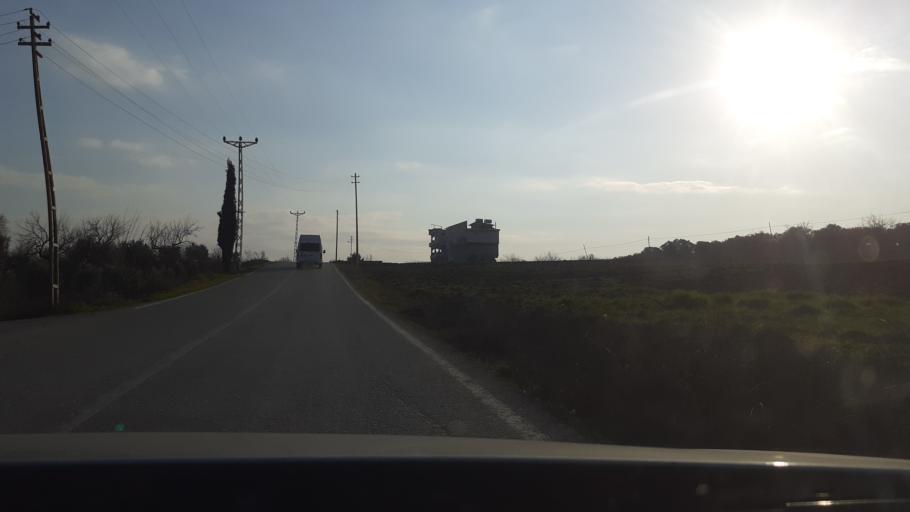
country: TR
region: Hatay
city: Boynuyogun
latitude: 36.1364
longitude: 36.3134
